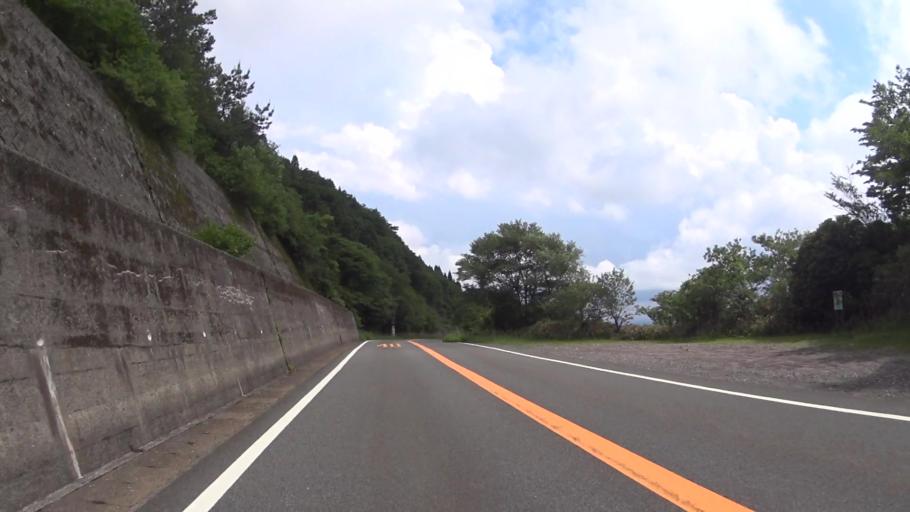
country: JP
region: Kumamoto
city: Aso
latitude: 33.0874
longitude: 131.1946
